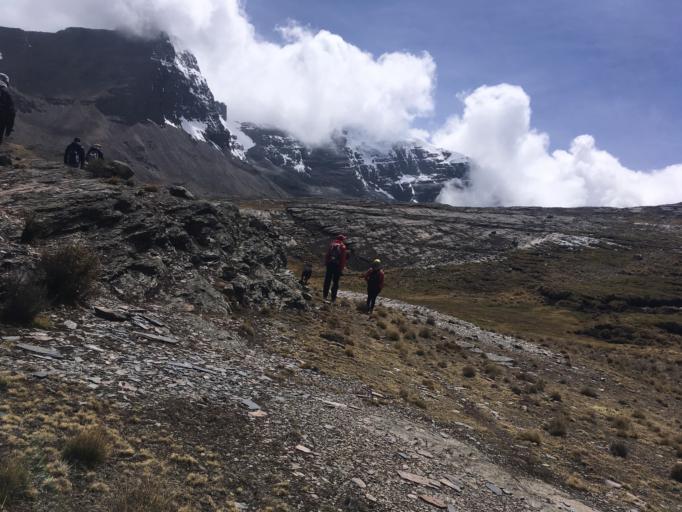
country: BO
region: La Paz
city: La Paz
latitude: -16.3965
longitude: -67.9672
